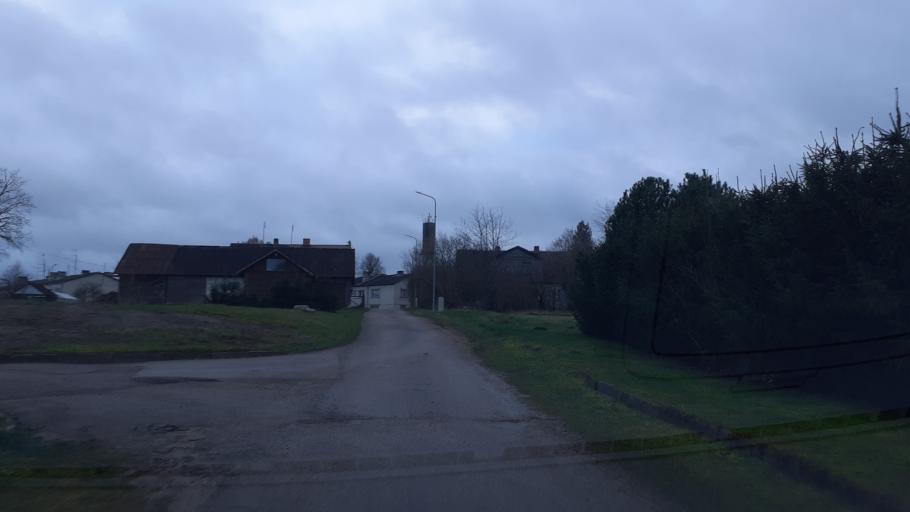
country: LV
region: Talsu Rajons
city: Stende
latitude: 57.0678
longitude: 22.2883
